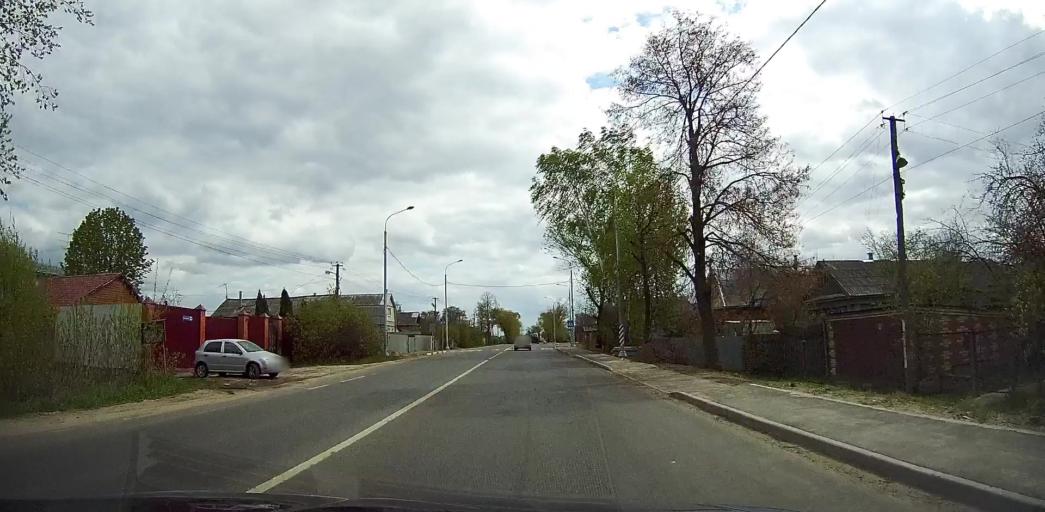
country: RU
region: Moskovskaya
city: Beloozerskiy
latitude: 55.4491
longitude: 38.4453
